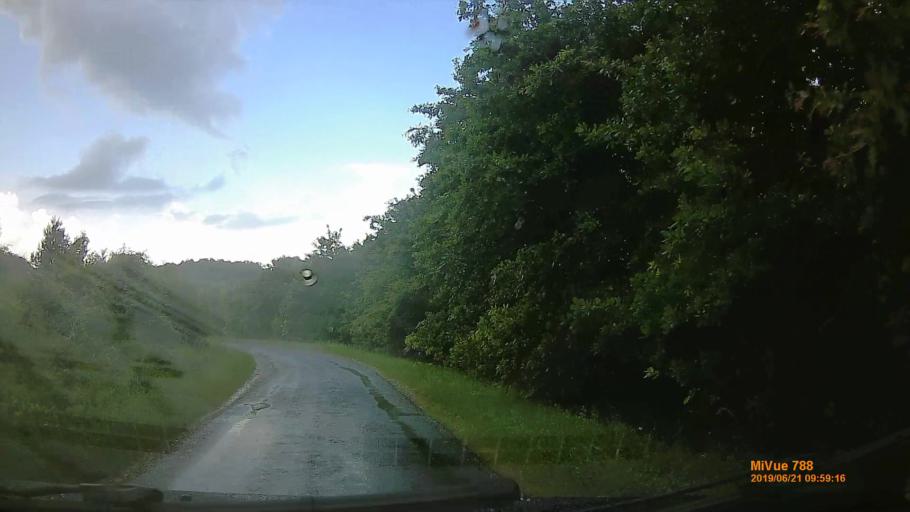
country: HU
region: Baranya
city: Buekkoesd
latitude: 46.2126
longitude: 17.9709
